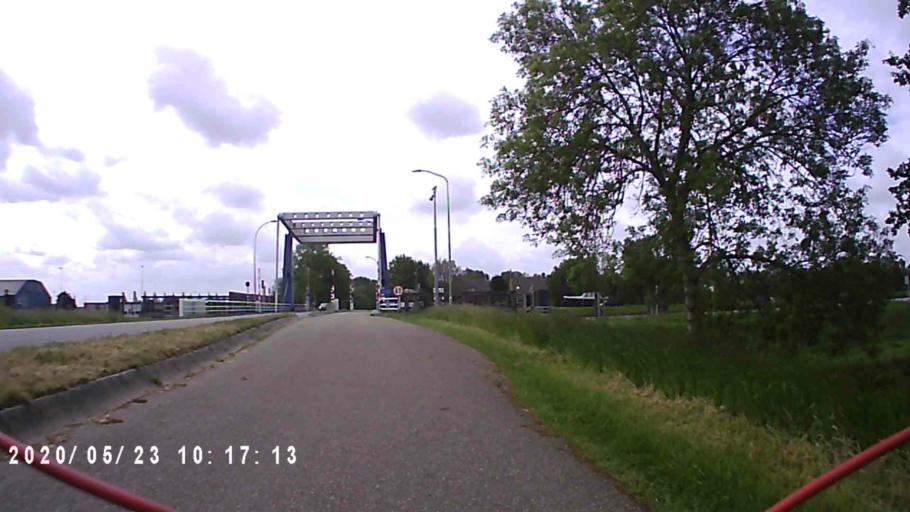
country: NL
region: Groningen
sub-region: Gemeente Appingedam
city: Appingedam
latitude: 53.3069
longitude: 6.8543
